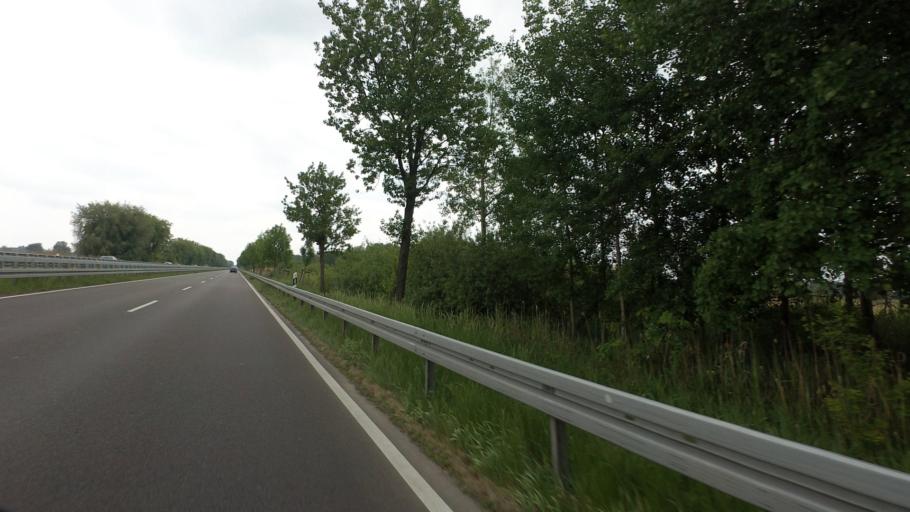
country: DE
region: Brandenburg
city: Peitz
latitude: 51.8417
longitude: 14.3879
